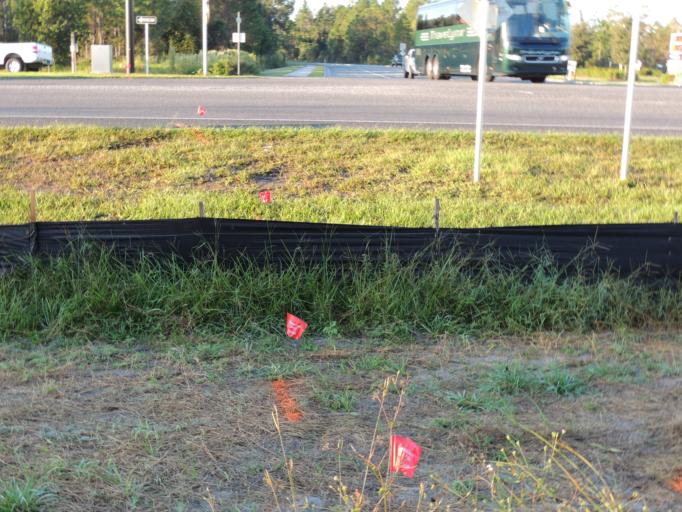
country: US
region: Florida
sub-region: Osceola County
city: Saint Cloud
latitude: 28.1925
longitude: -81.1545
